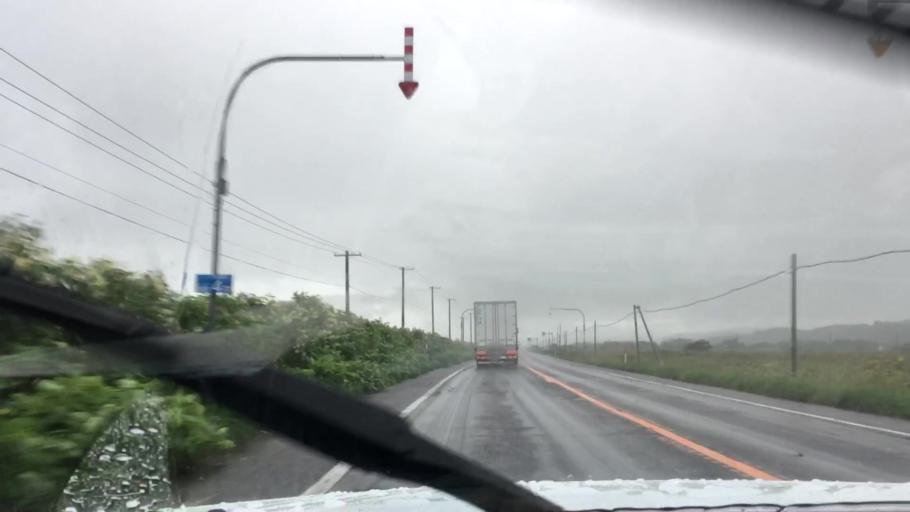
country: JP
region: Hokkaido
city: Niseko Town
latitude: 42.4276
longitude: 140.3167
